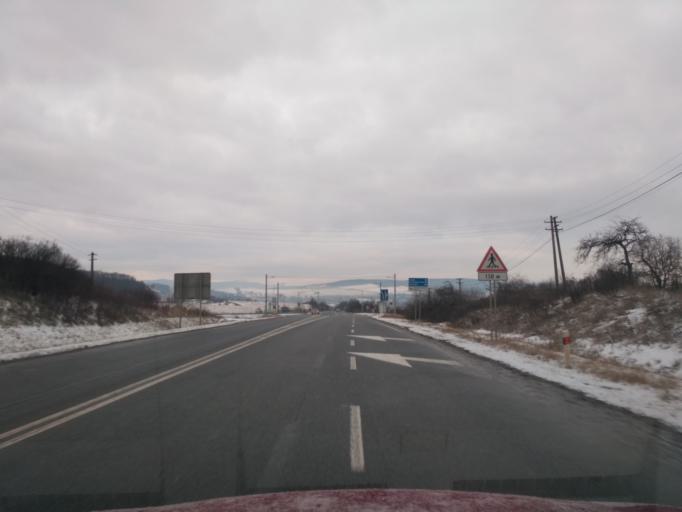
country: SK
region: Presovsky
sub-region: Okres Presov
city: Presov
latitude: 49.0013
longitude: 21.1932
